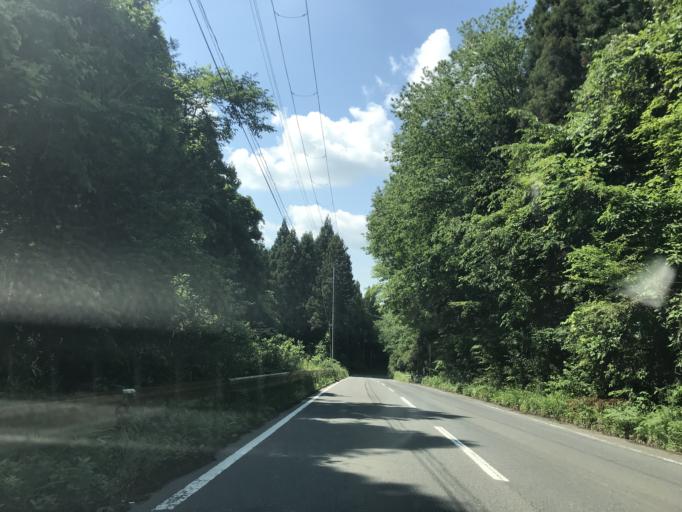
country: JP
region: Miyagi
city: Furukawa
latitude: 38.7122
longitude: 140.9421
